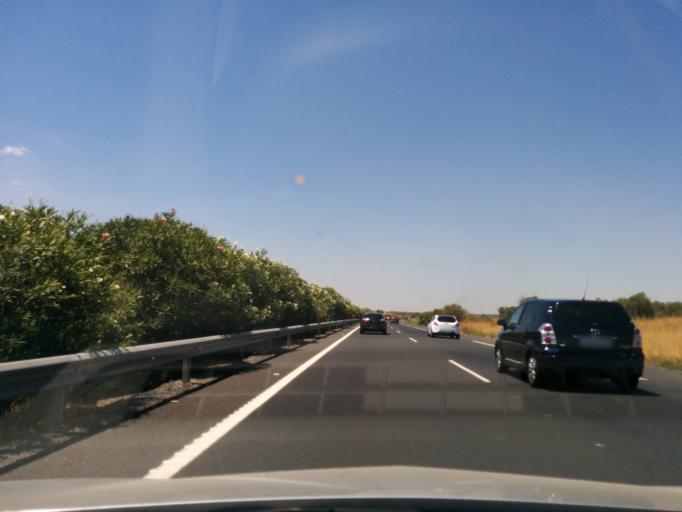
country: ES
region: Andalusia
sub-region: Provincia de Huelva
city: Bonares
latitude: 37.3420
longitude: -6.6865
